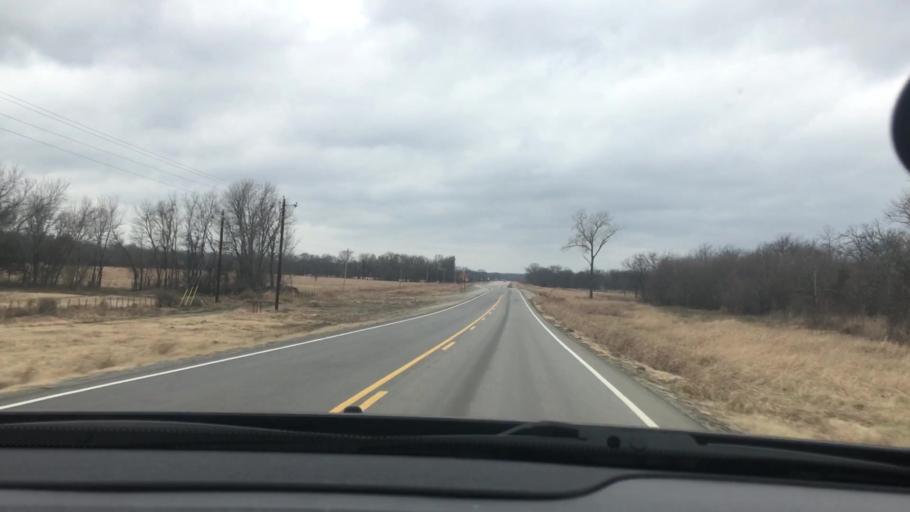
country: US
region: Oklahoma
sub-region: Atoka County
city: Atoka
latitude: 34.3748
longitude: -96.3035
